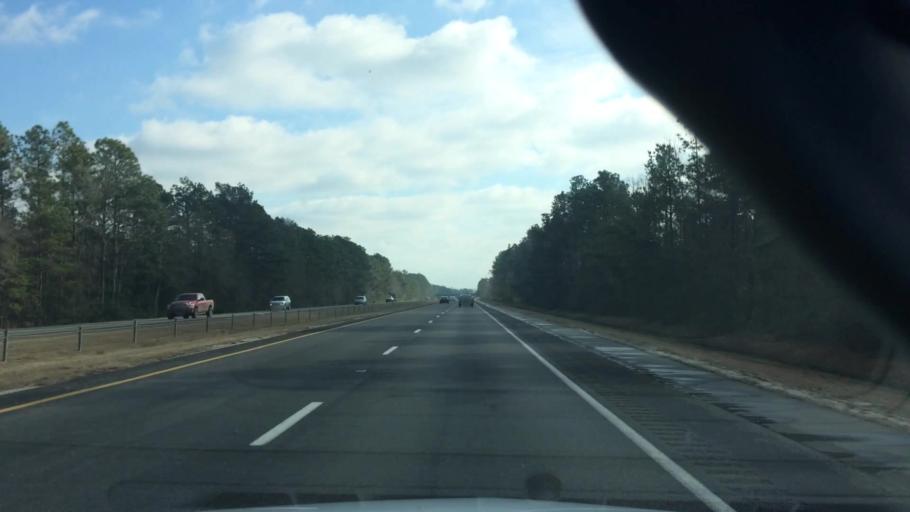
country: US
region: North Carolina
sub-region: Pender County
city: Burgaw
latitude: 34.6194
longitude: -77.9282
